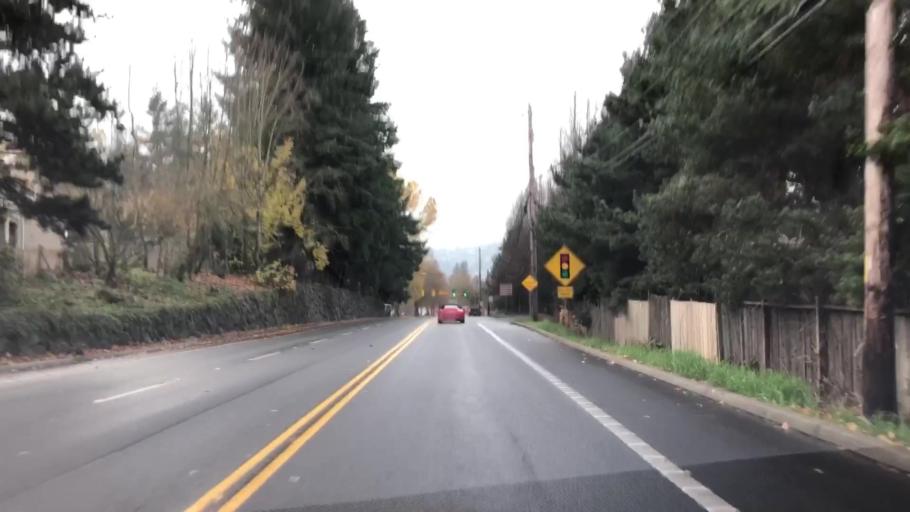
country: US
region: Washington
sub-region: King County
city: Woodinville
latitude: 47.7577
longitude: -122.1482
